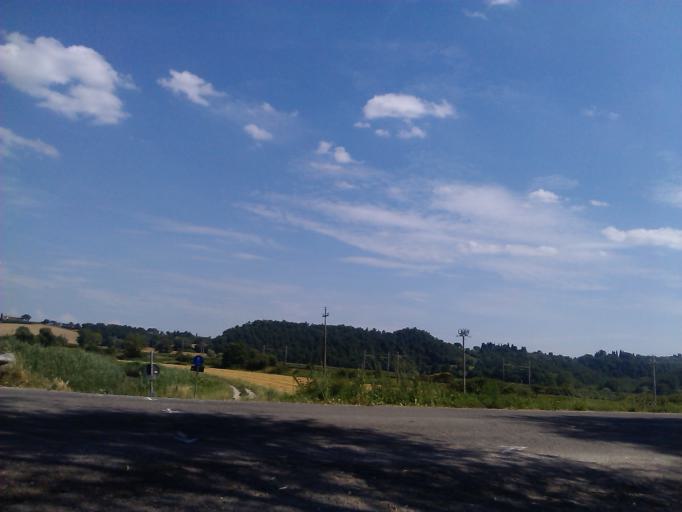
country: IT
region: Tuscany
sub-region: Provincia di Siena
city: Chiusi
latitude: 43.0540
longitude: 11.9384
